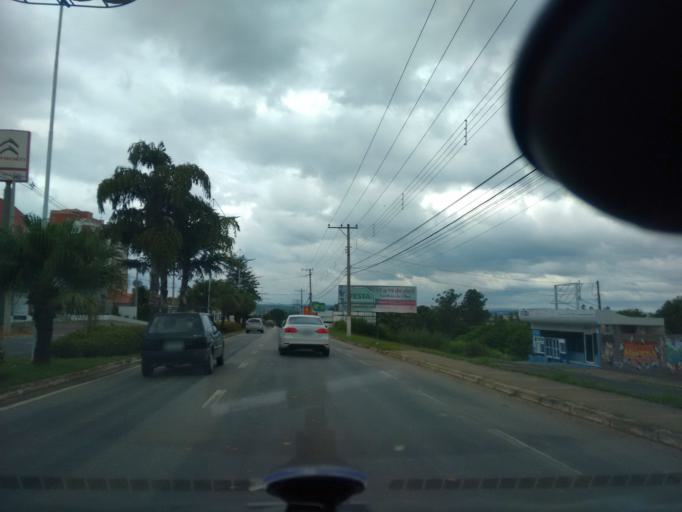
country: BR
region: Sao Paulo
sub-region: Indaiatuba
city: Indaiatuba
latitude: -23.0857
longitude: -47.1840
